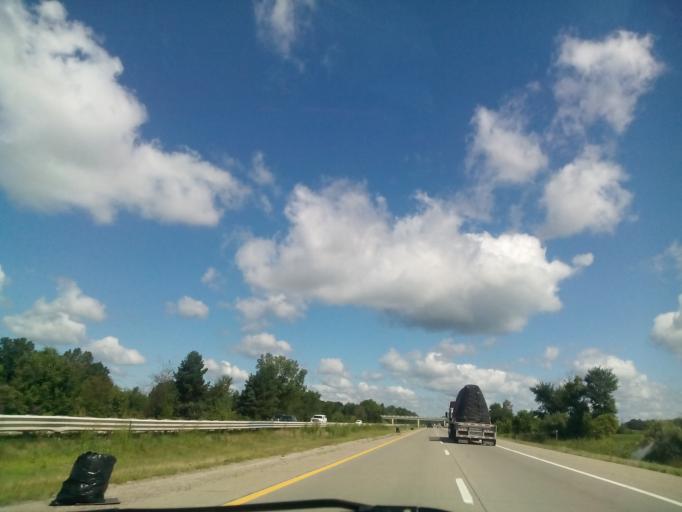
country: US
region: Michigan
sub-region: Genesee County
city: Lake Fenton
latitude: 42.8811
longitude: -83.7388
